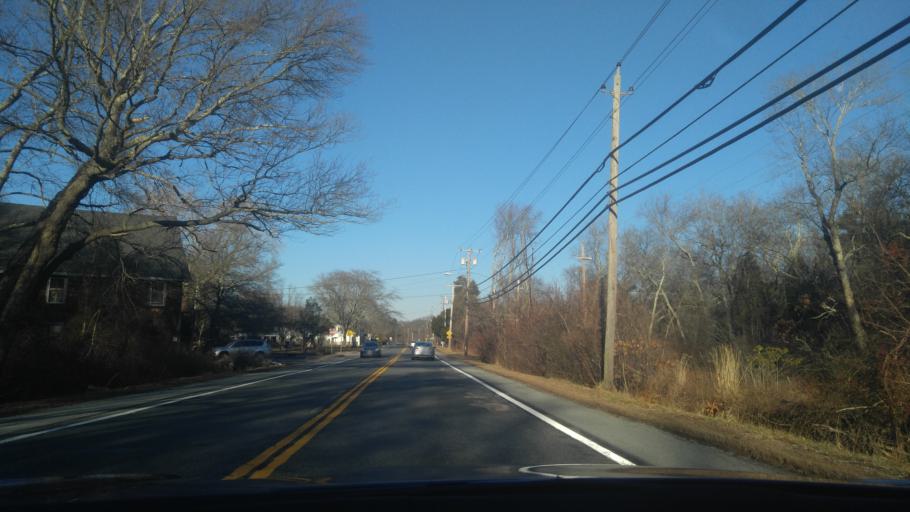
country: US
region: Rhode Island
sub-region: Washington County
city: North Kingstown
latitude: 41.5067
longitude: -71.4262
